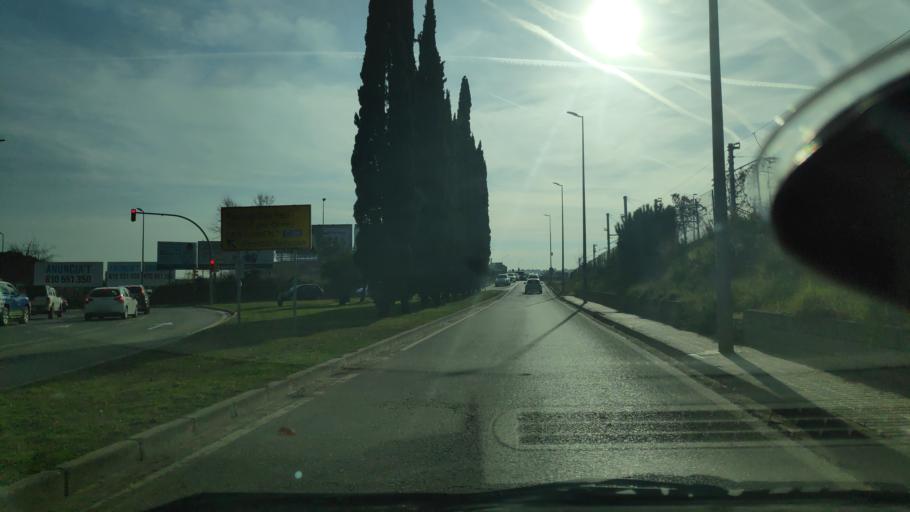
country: ES
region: Catalonia
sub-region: Provincia de Barcelona
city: Sant Quirze del Valles
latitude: 41.5375
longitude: 2.0948
